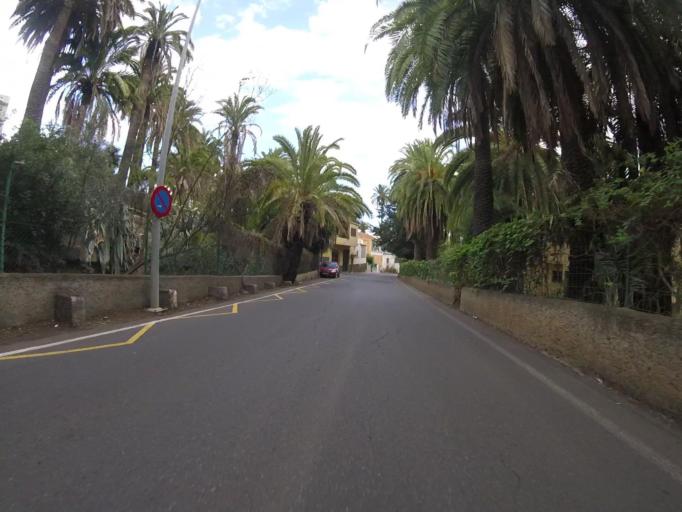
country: ES
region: Canary Islands
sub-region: Provincia de Las Palmas
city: Santa Brigida
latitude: 28.0419
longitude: -15.4896
